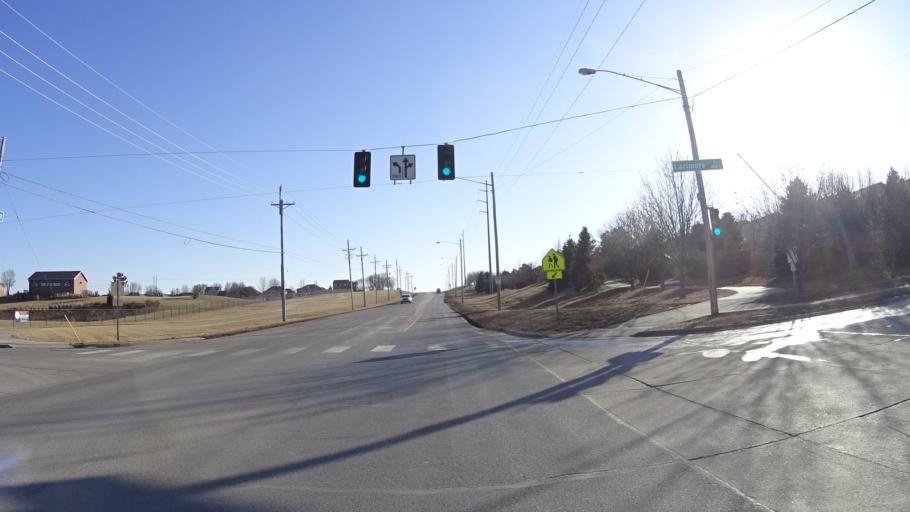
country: US
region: Nebraska
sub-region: Douglas County
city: Bennington
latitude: 41.3021
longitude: -96.1390
